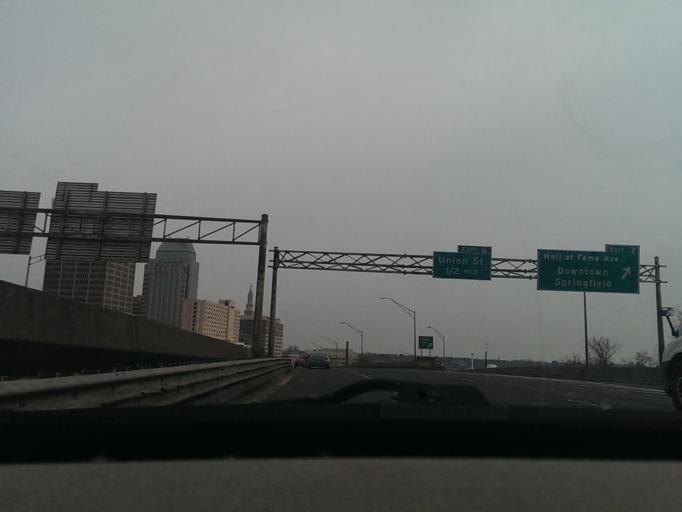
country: US
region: Massachusetts
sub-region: Hampden County
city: Springfield
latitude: 42.1037
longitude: -72.5975
